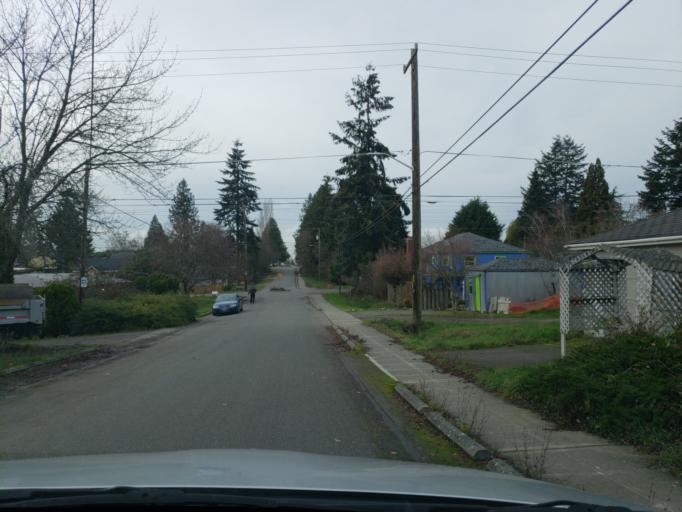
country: US
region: Washington
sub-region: King County
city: Shoreline
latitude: 47.6996
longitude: -122.3503
